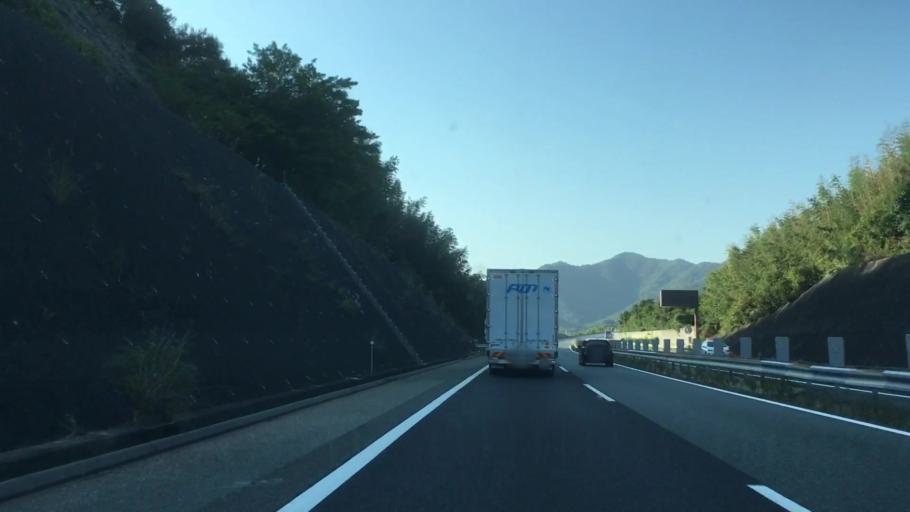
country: JP
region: Yamaguchi
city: Ogori-shimogo
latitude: 34.0906
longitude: 131.4588
